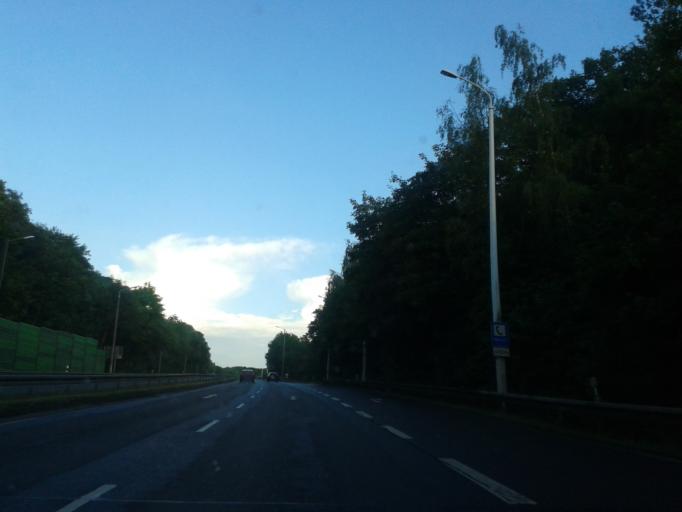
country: DE
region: Saxony
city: Markkleeberg
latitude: 51.3041
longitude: 12.3691
